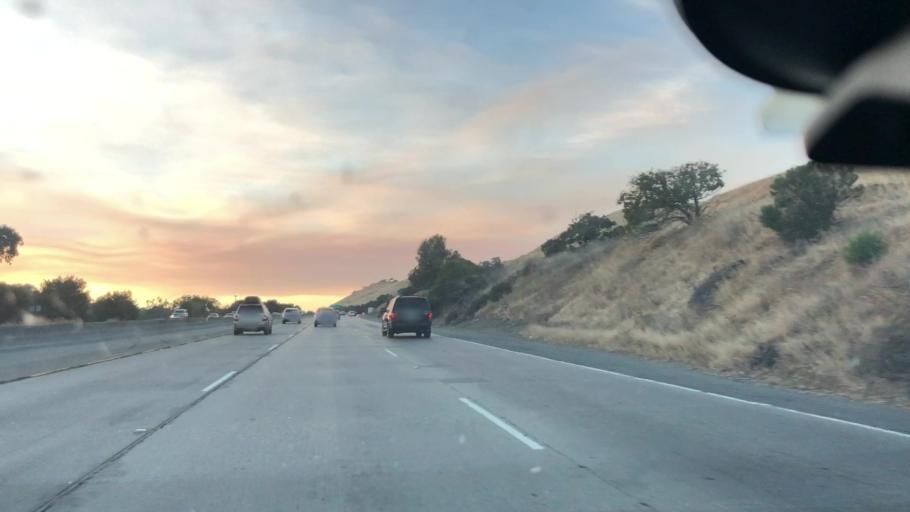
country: US
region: California
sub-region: Alameda County
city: Pleasanton
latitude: 37.6066
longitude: -121.8728
